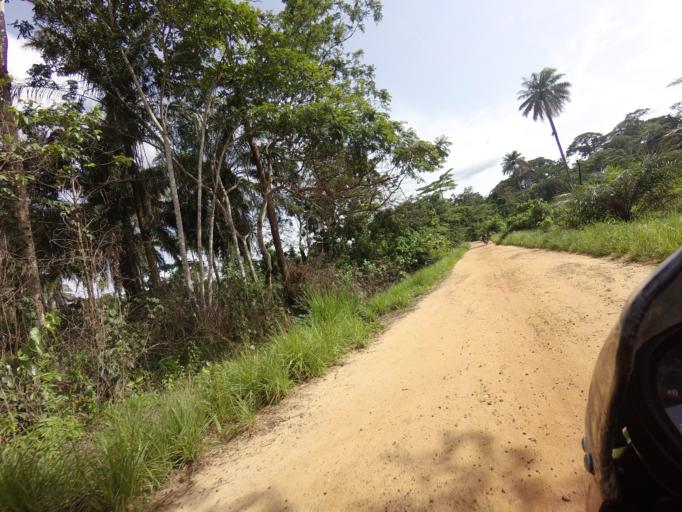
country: SL
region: Eastern Province
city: Jojoima
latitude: 7.8676
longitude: -10.7978
